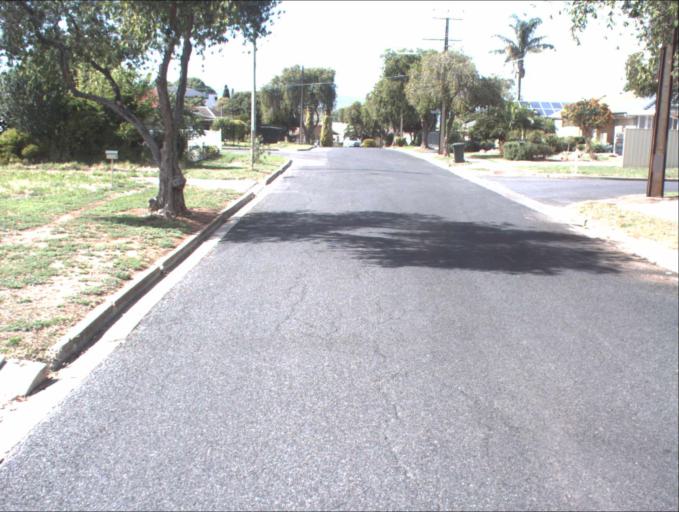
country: AU
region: South Australia
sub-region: Port Adelaide Enfield
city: Gilles Plains
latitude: -34.8670
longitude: 138.6521
